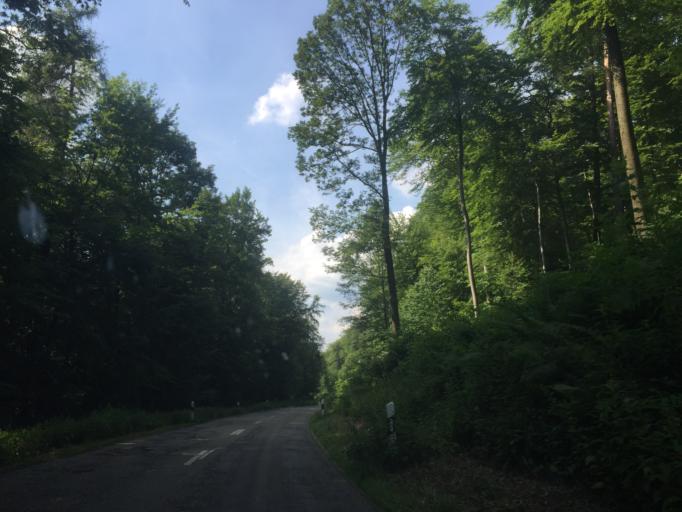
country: DE
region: Baden-Wuerttemberg
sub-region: Karlsruhe Region
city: Heidelberg
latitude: 49.3873
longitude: 8.7163
